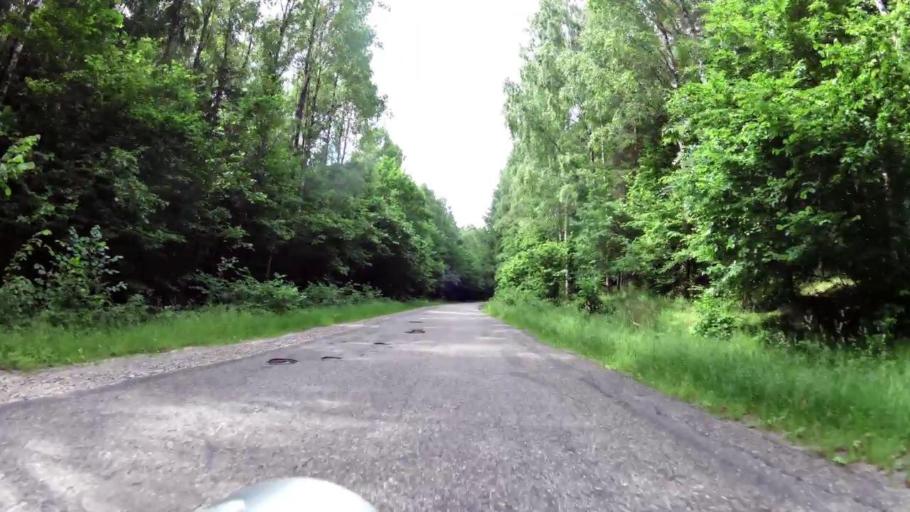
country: PL
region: West Pomeranian Voivodeship
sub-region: Powiat szczecinecki
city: Bialy Bor
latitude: 53.9604
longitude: 16.7336
